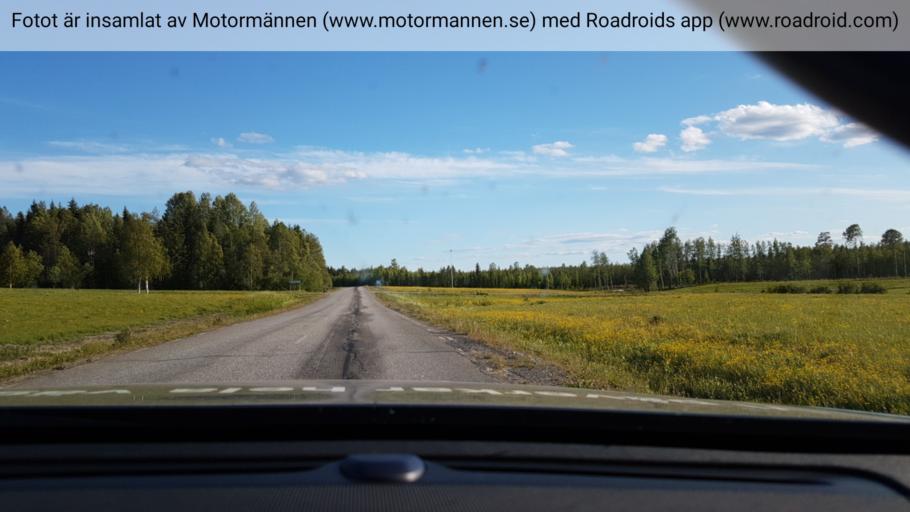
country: SE
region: Vaesterbotten
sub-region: Vannas Kommun
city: Vannasby
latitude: 64.0434
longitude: 19.9327
